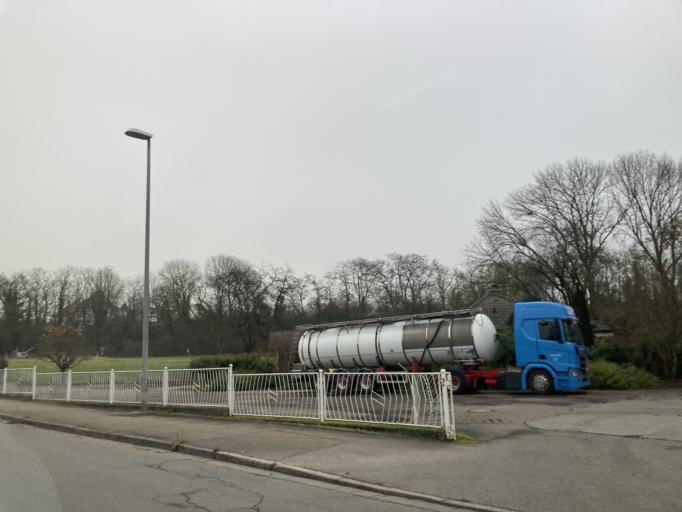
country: DE
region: Baden-Wuerttemberg
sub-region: Freiburg Region
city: Neuenburg am Rhein
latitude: 47.8079
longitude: 7.5614
